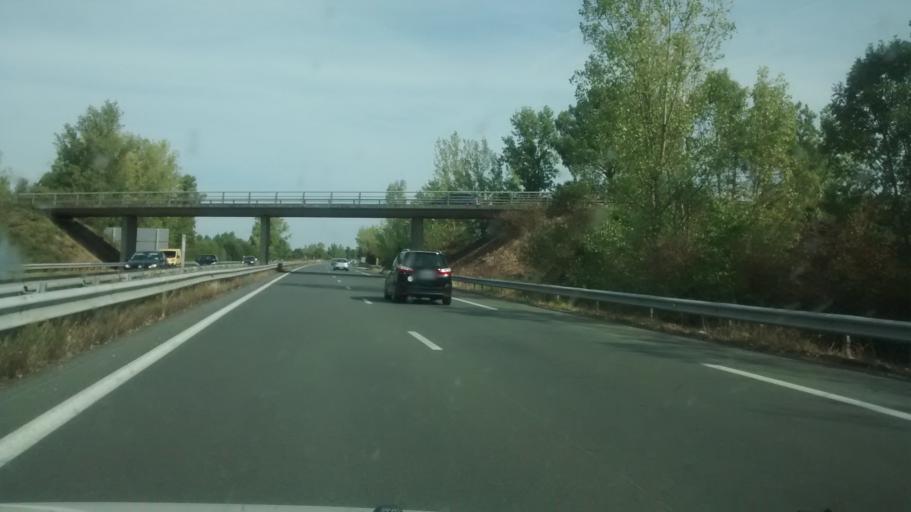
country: FR
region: Aquitaine
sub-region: Departement du Lot-et-Garonne
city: Damazan
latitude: 44.2933
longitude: 0.2624
